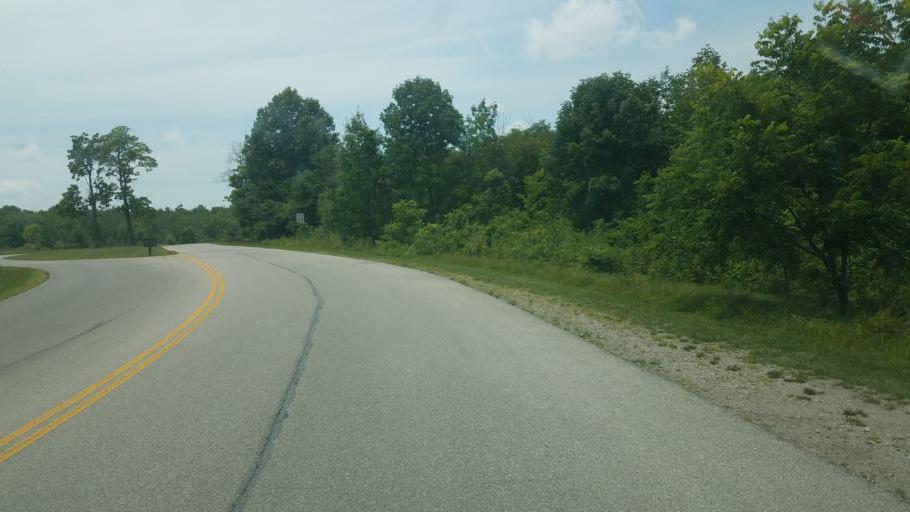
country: US
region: Ohio
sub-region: Delaware County
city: Lewis Center
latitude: 40.1528
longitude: -83.0190
